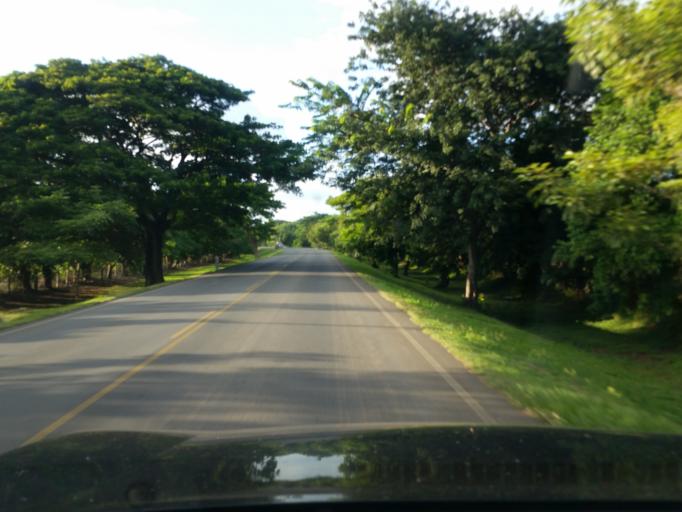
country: NI
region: Granada
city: Nandaime
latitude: 11.7440
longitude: -86.0246
